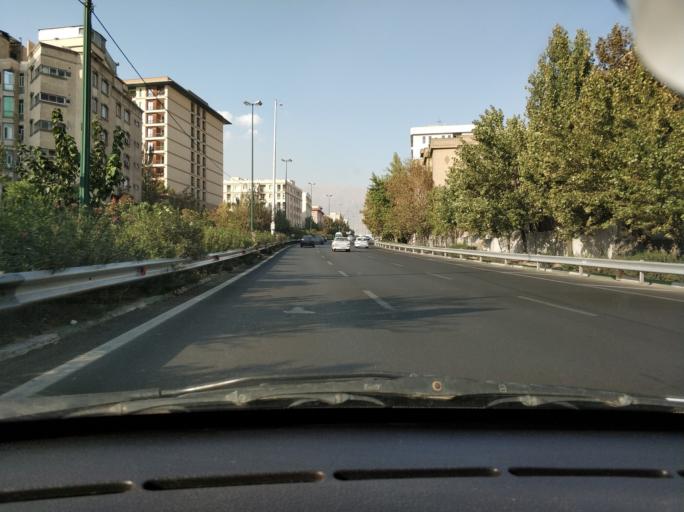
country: IR
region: Tehran
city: Tajrish
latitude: 35.7637
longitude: 51.4668
